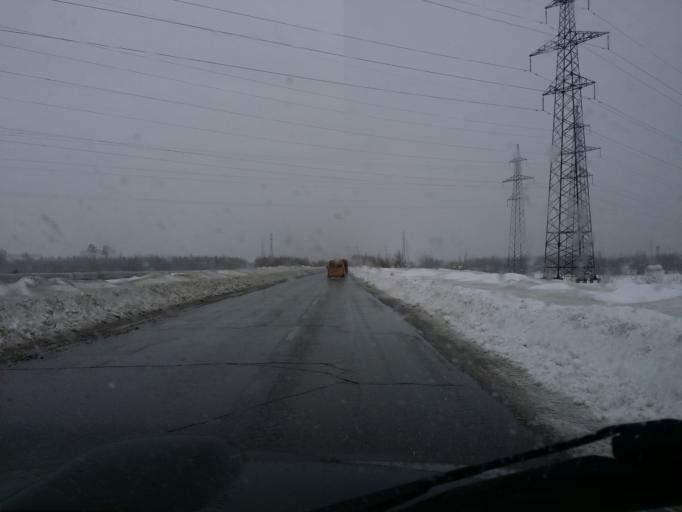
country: RU
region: Khanty-Mansiyskiy Avtonomnyy Okrug
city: Izluchinsk
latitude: 60.9697
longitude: 76.8892
